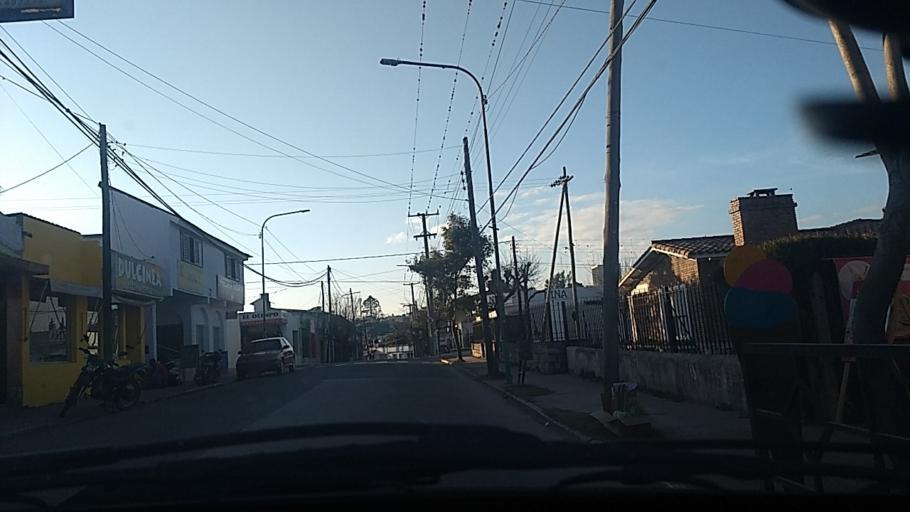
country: AR
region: Cordoba
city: Salsipuedes
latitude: -31.1372
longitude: -64.2959
